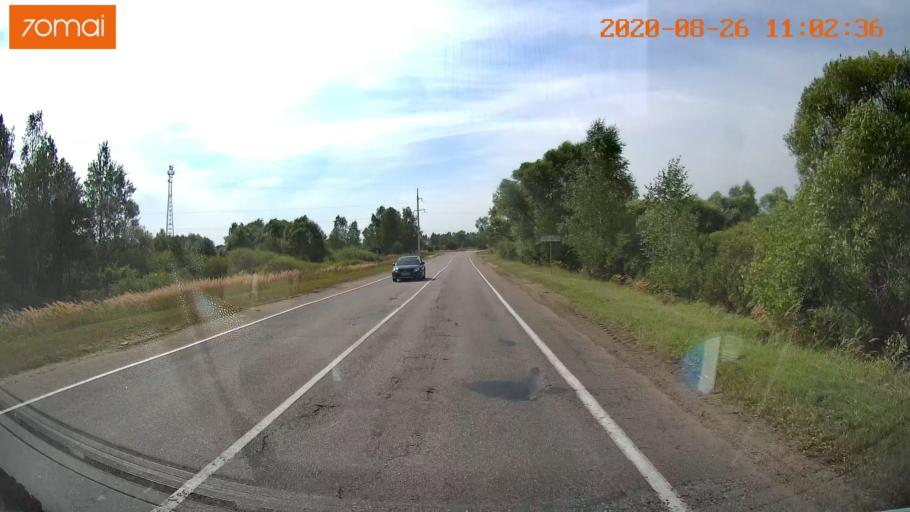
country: RU
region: Rjazan
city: Izhevskoye
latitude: 54.5484
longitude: 41.2233
